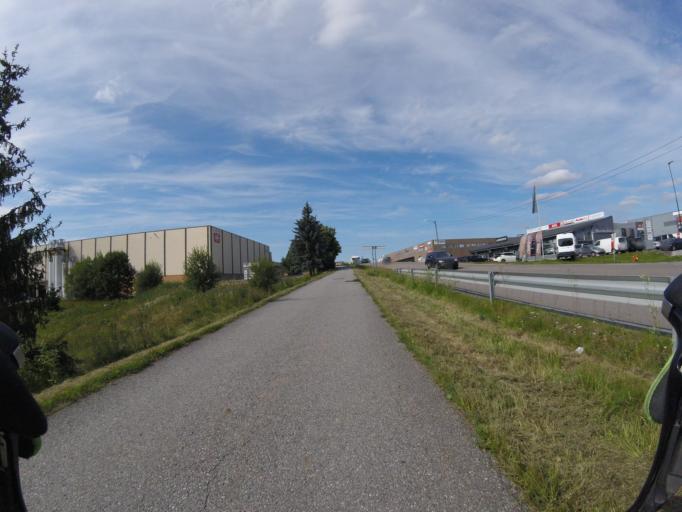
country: NO
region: Akershus
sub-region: Skedsmo
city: Lillestrom
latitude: 59.9760
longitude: 11.0025
